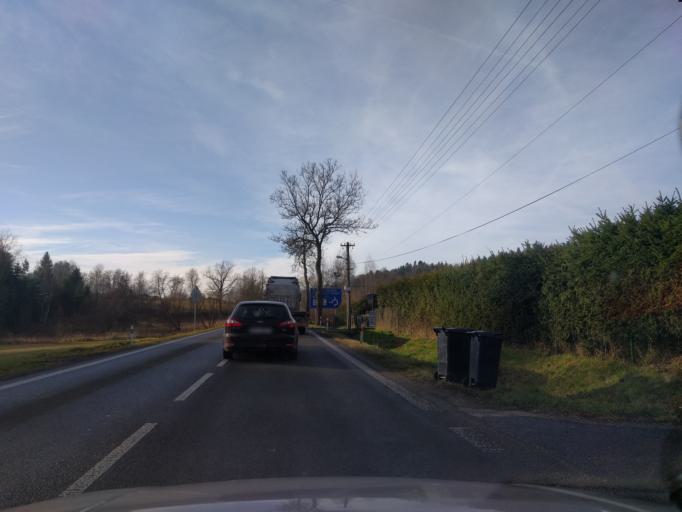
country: CZ
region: Liberecky
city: Mnisek
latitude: 50.8202
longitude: 15.0401
